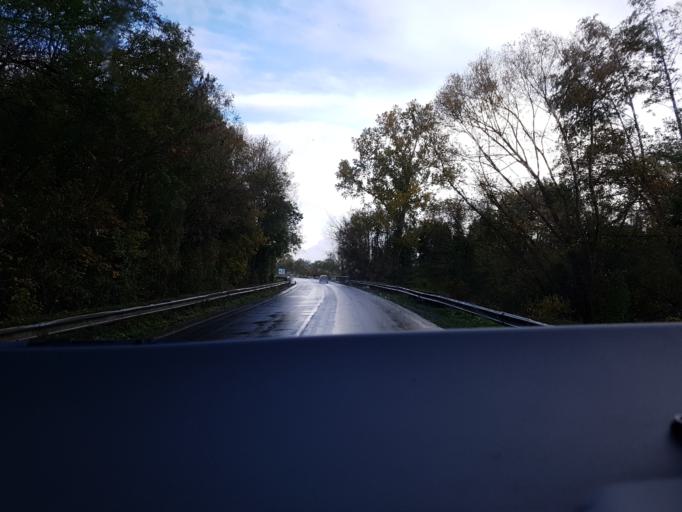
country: FR
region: Poitou-Charentes
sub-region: Departement de la Charente-Maritime
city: Saint-Jean-d'Angely
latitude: 45.9359
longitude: -0.5245
